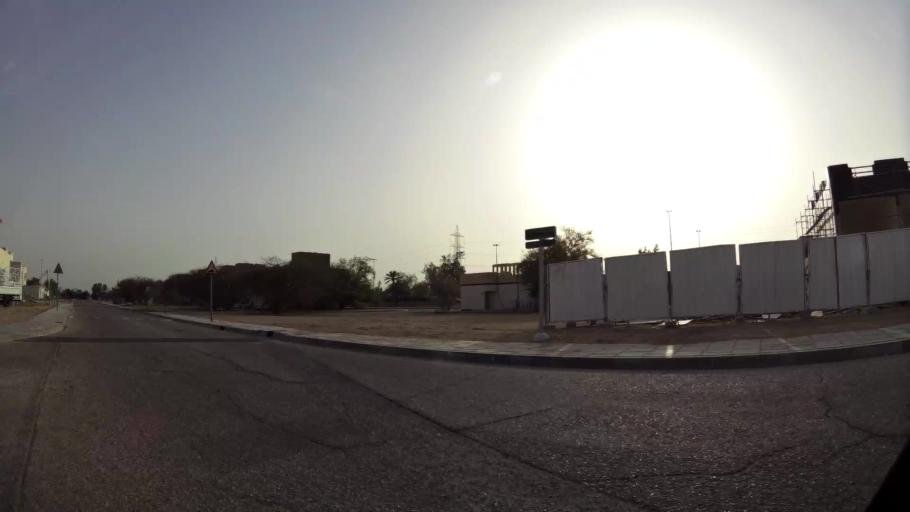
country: AE
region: Abu Dhabi
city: Al Ain
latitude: 24.1254
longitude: 55.7131
